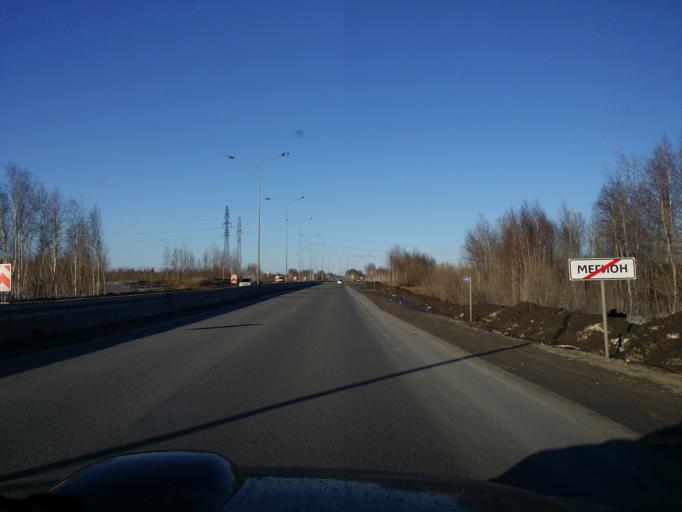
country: RU
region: Khanty-Mansiyskiy Avtonomnyy Okrug
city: Megion
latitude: 61.0497
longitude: 76.1350
